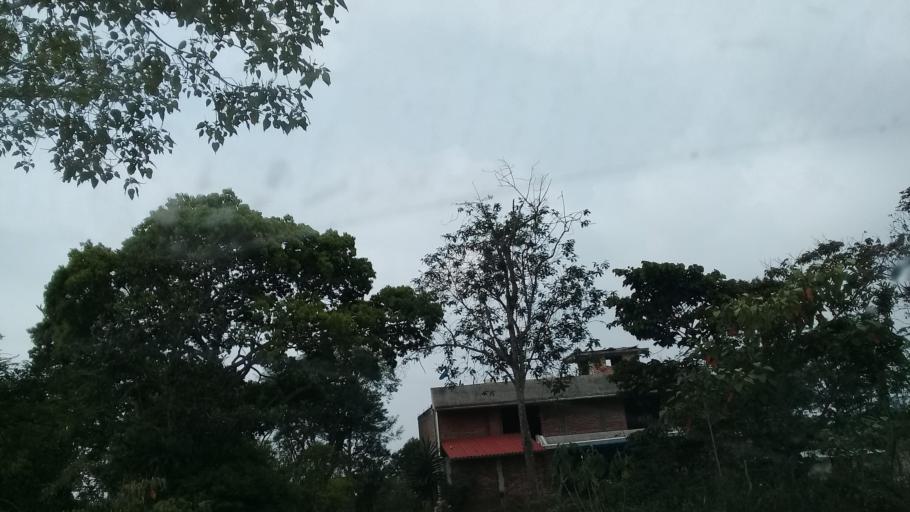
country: MX
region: Veracruz
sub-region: Xalapa
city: Fraccionamiento las Fuentes
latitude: 19.4944
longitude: -96.8950
